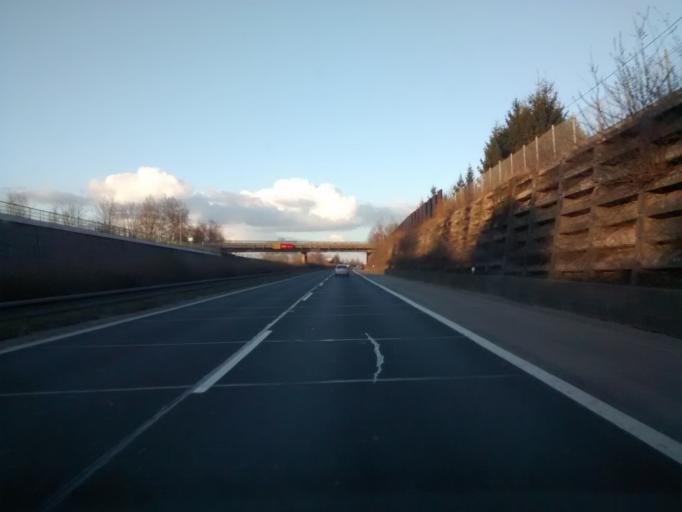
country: CZ
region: Praha
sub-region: Praha 20
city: Horni Pocernice
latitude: 50.1019
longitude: 14.6144
